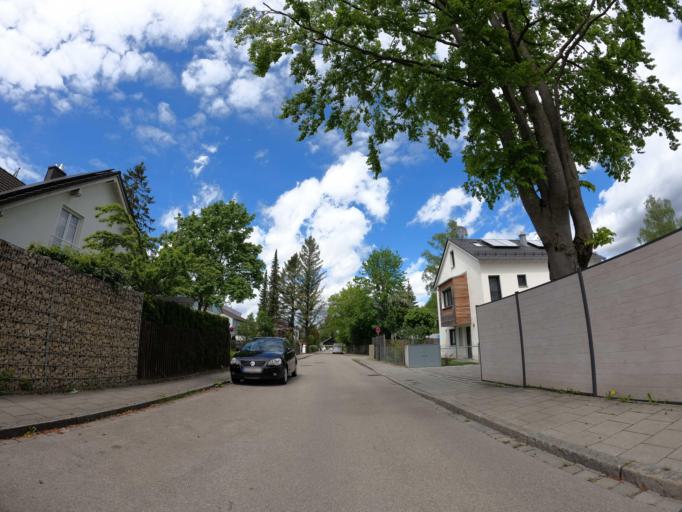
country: DE
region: Bavaria
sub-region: Upper Bavaria
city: Ottobrunn
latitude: 48.0674
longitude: 11.6749
